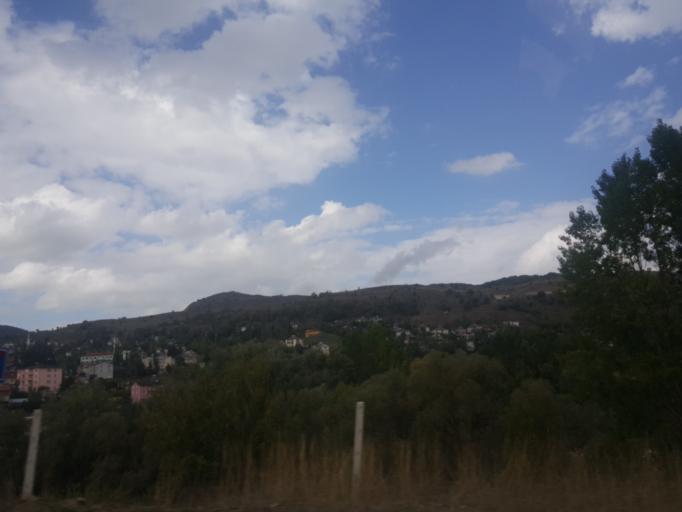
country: TR
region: Tokat
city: Bereketli
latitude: 40.5352
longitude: 37.2972
